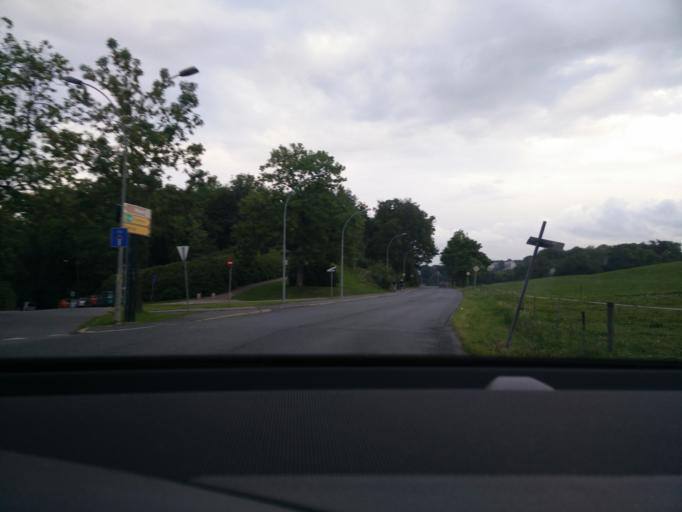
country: NO
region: Oslo
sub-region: Oslo
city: Sjolyststranda
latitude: 59.9134
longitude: 10.6808
